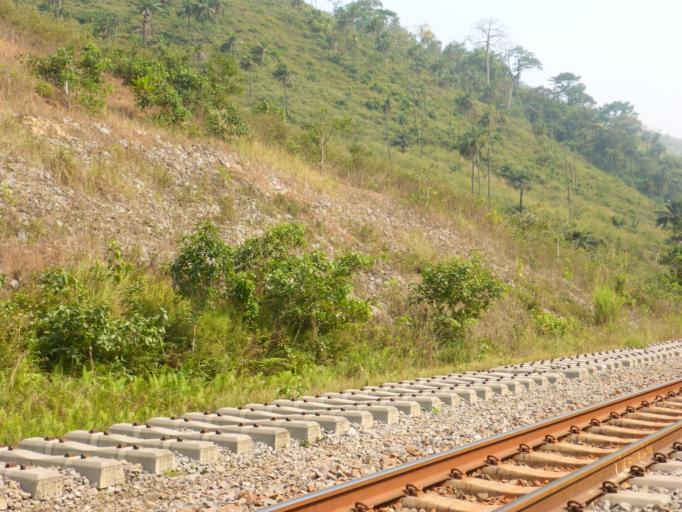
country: SL
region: Northern Province
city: Bumbuna
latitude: 8.9442
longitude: -11.7424
